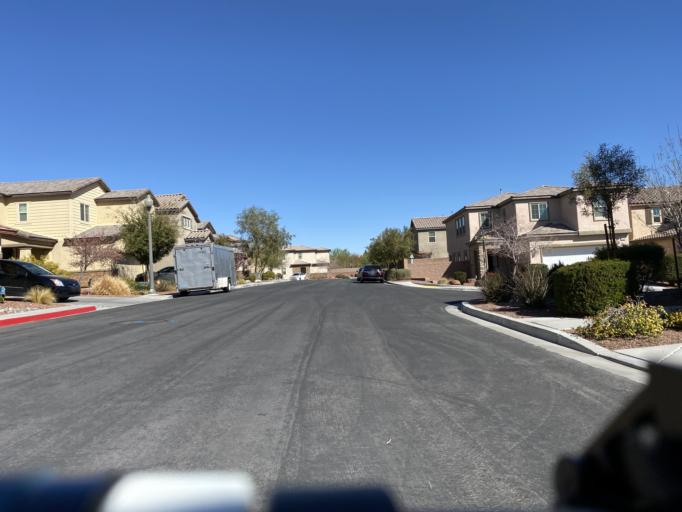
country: US
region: Nevada
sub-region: Clark County
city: Summerlin South
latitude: 36.2907
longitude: -115.3226
